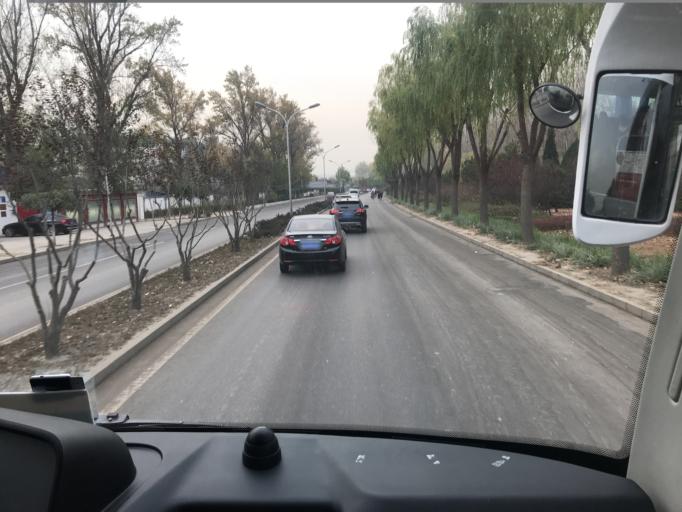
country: CN
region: Beijing
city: Sujiatuo
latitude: 40.0969
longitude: 116.2080
